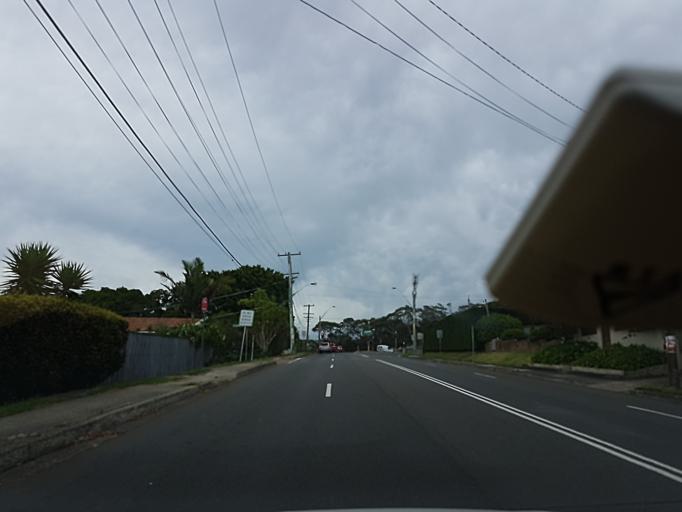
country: AU
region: New South Wales
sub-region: Warringah
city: Brookvale
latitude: -33.7561
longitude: 151.2639
